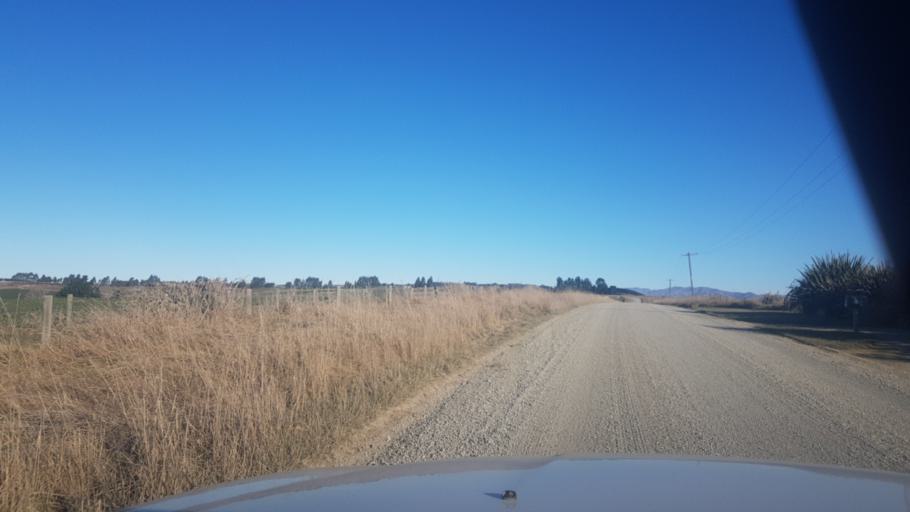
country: NZ
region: Canterbury
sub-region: Timaru District
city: Pleasant Point
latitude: -44.3507
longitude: 171.0722
